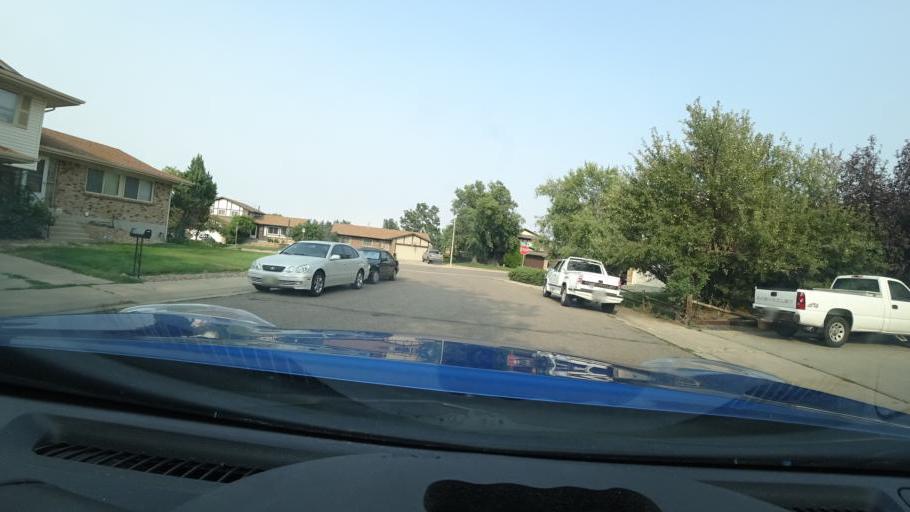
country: US
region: Colorado
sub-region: Adams County
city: Aurora
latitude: 39.6726
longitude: -104.7873
